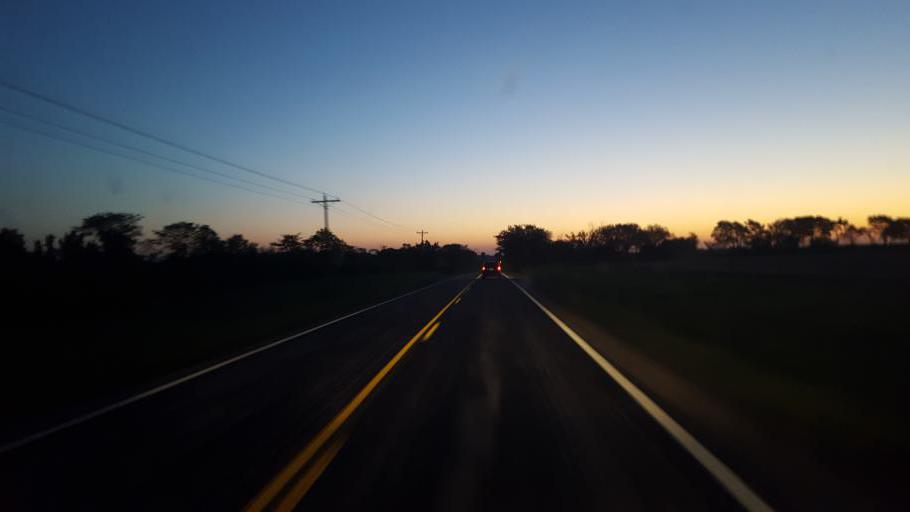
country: US
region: Missouri
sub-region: Mercer County
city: Princeton
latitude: 40.4211
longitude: -93.4884
